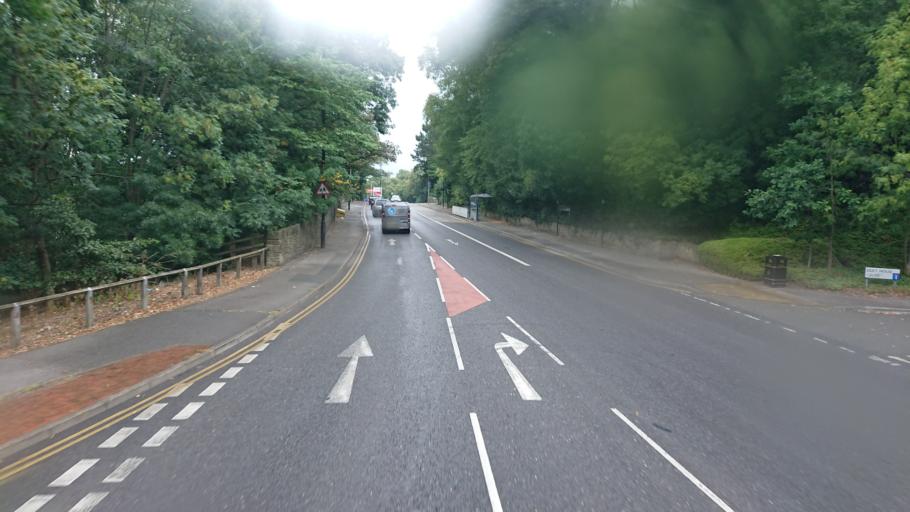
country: GB
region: England
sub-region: Sheffield
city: Sheffield
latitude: 53.3495
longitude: -1.4912
